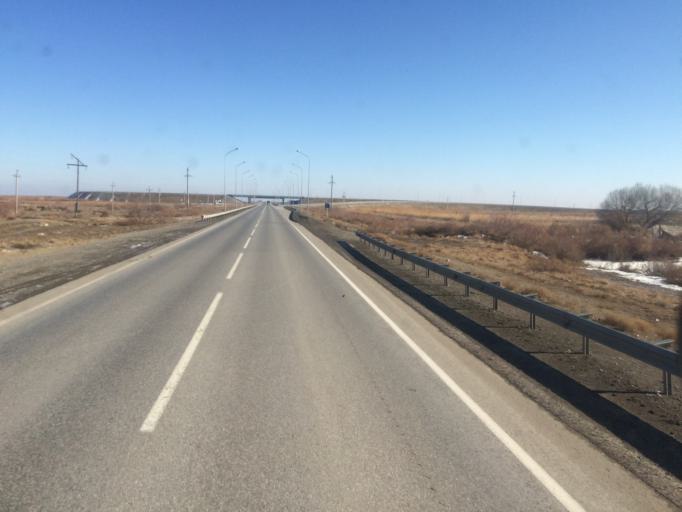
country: KZ
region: Qyzylorda
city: Terenozek
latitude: 44.8817
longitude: 65.1181
